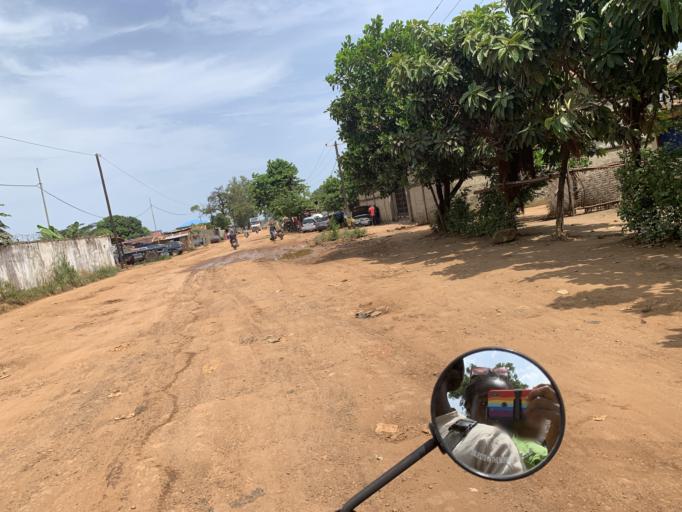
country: SL
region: Western Area
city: Hastings
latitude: 8.3984
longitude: -13.1404
